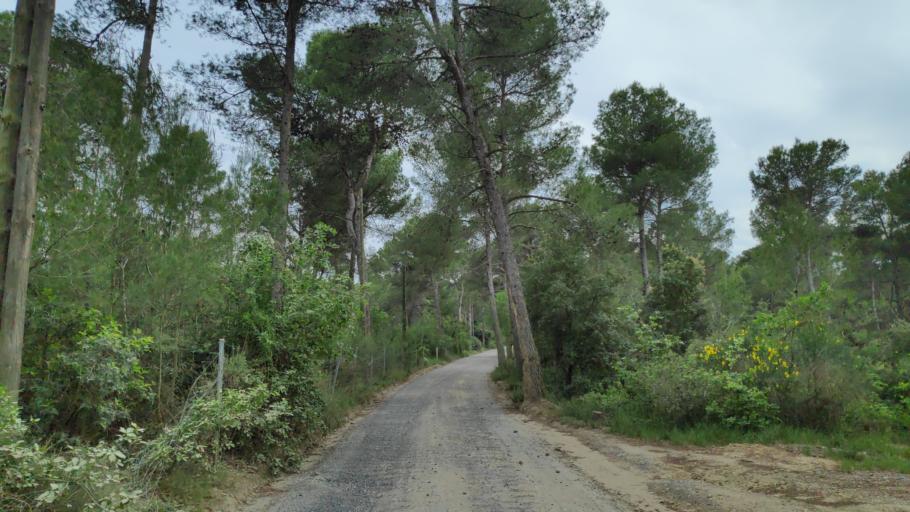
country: ES
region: Catalonia
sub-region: Provincia de Barcelona
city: Sant Quirze del Valles
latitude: 41.5125
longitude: 2.0827
